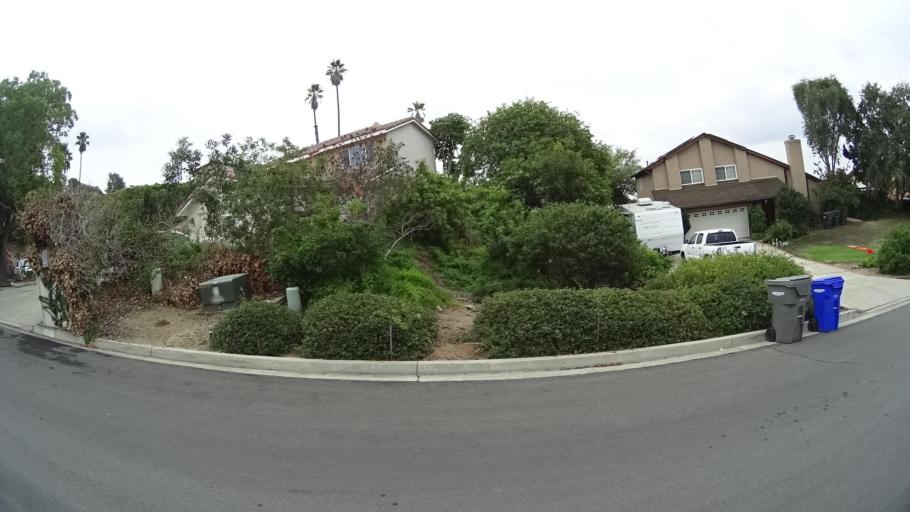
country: US
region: California
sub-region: San Diego County
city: Spring Valley
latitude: 32.7619
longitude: -116.9904
